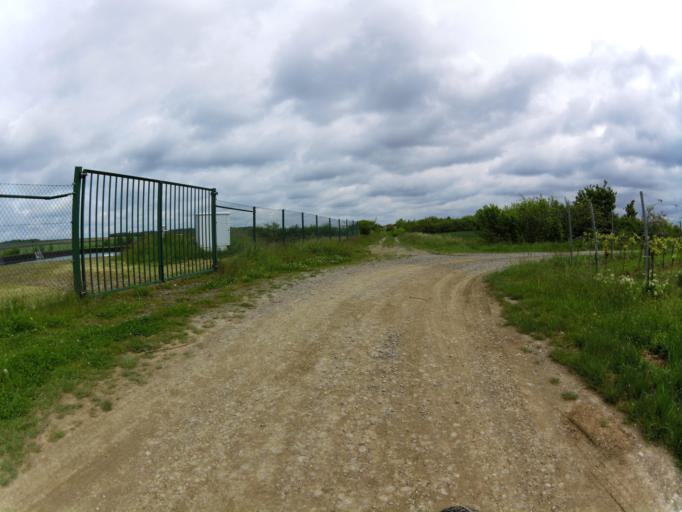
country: DE
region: Bavaria
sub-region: Regierungsbezirk Unterfranken
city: Volkach
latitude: 49.8781
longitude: 10.2150
